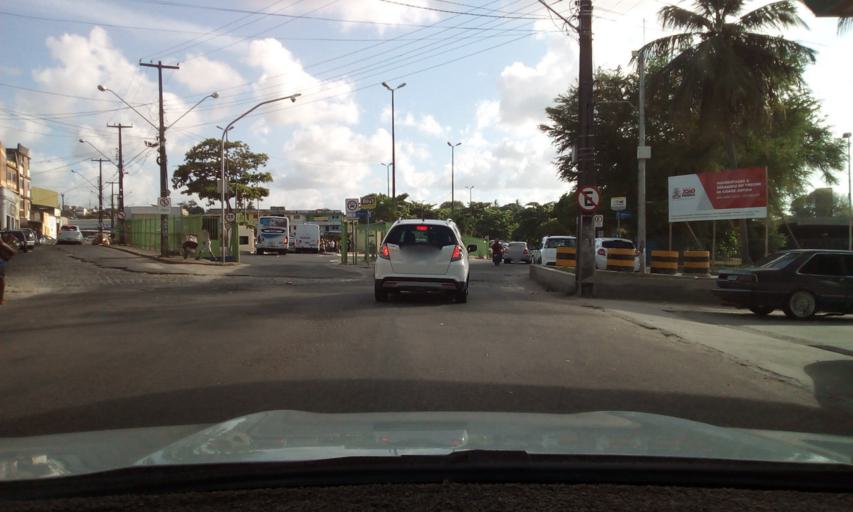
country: BR
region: Paraiba
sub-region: Joao Pessoa
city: Joao Pessoa
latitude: -7.1169
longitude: -34.8898
